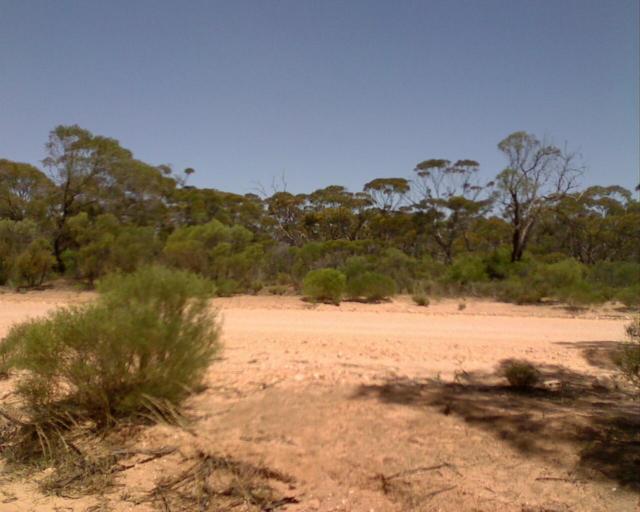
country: AU
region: South Australia
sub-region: Kimba
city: Caralue
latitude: -32.9452
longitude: 135.2710
